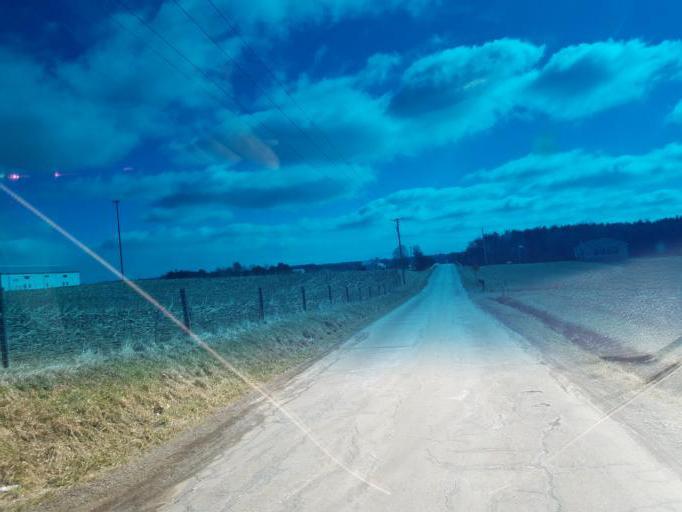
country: US
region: Ohio
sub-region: Richland County
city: Lexington
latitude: 40.5876
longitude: -82.6000
